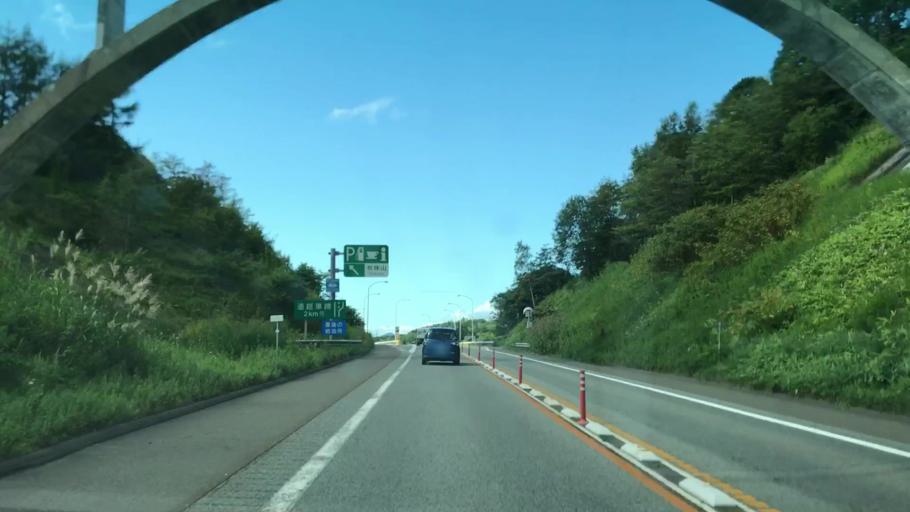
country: JP
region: Hokkaido
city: Date
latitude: 42.4617
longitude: 140.9109
